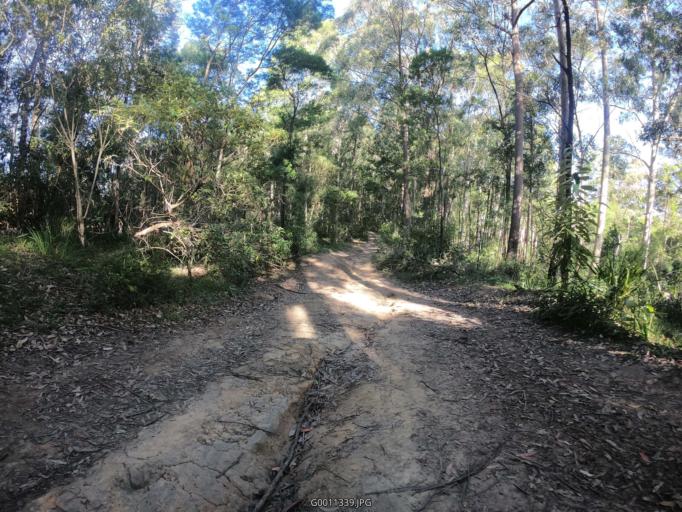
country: AU
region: New South Wales
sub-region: Lake Macquarie Shire
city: Cooranbong
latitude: -33.0246
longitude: 151.2997
